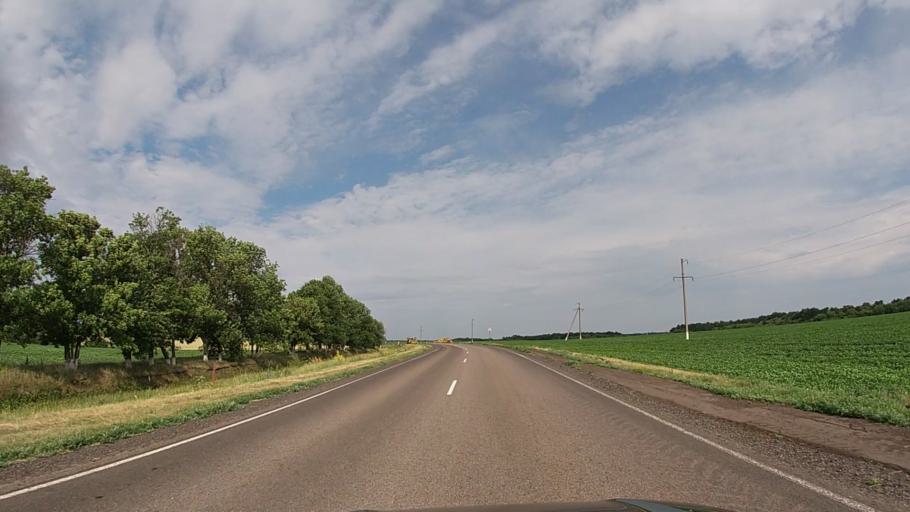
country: RU
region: Belgorod
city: Krasnaya Yaruga
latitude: 50.8076
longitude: 35.5417
